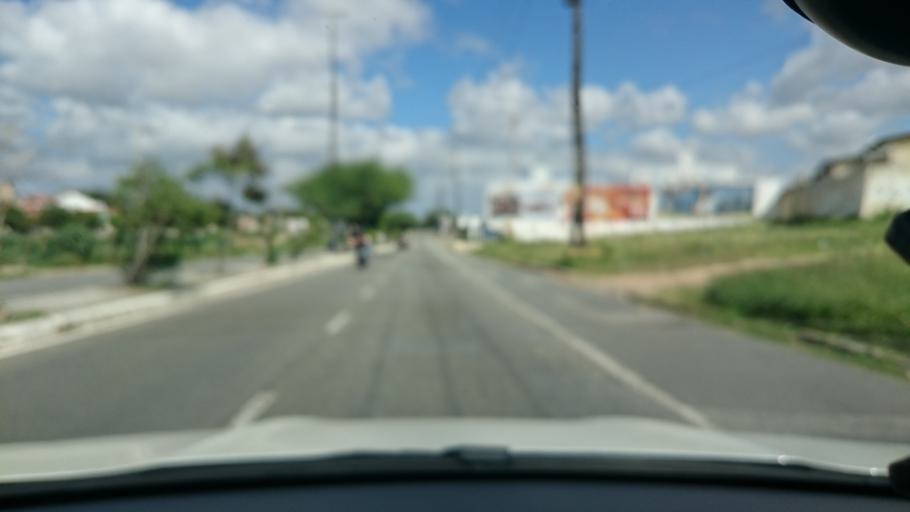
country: BR
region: Paraiba
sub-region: Campina Grande
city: Campina Grande
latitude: -7.2302
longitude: -35.9075
